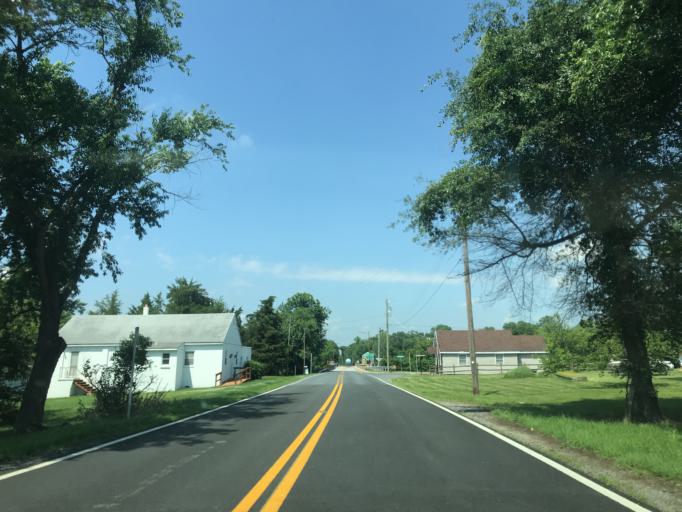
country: US
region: Maryland
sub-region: Dorchester County
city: Hurlock
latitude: 38.5752
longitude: -75.7961
